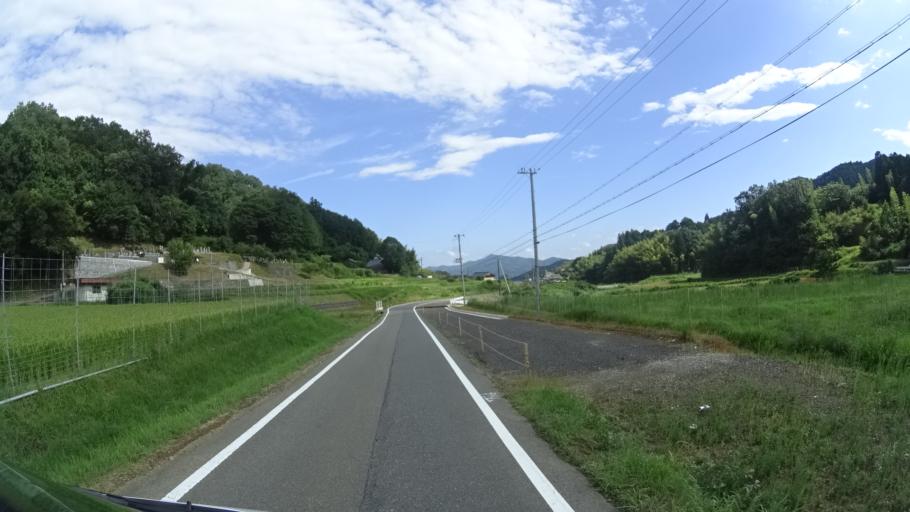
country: JP
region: Kyoto
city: Fukuchiyama
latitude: 35.3391
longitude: 135.1684
